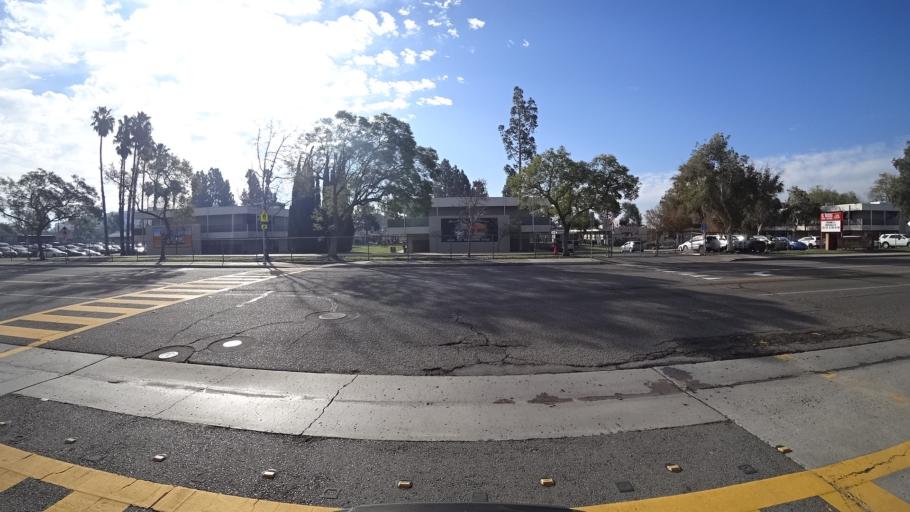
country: US
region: California
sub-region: Orange County
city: Villa Park
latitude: 33.7915
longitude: -117.8110
